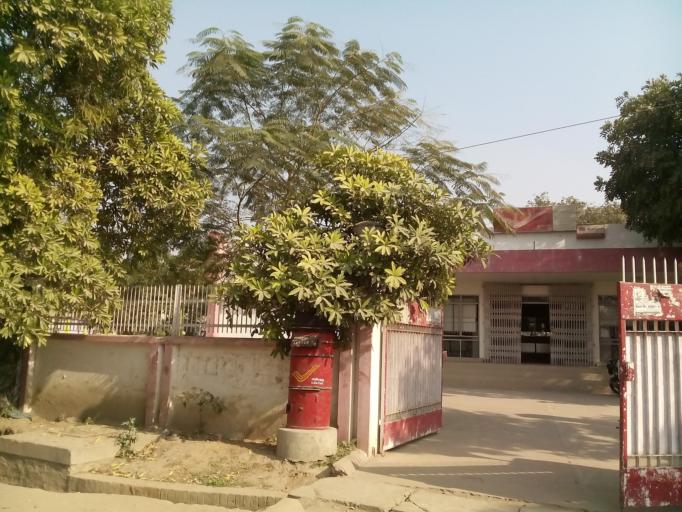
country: IN
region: Uttar Pradesh
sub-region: Kanpur
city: Kanpur
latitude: 26.4186
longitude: 80.3237
